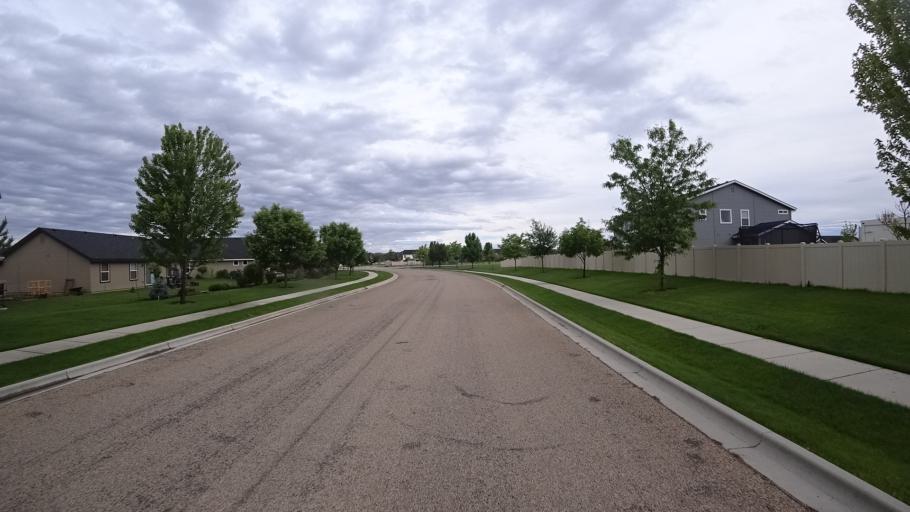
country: US
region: Idaho
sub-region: Ada County
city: Star
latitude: 43.6994
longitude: -116.5051
